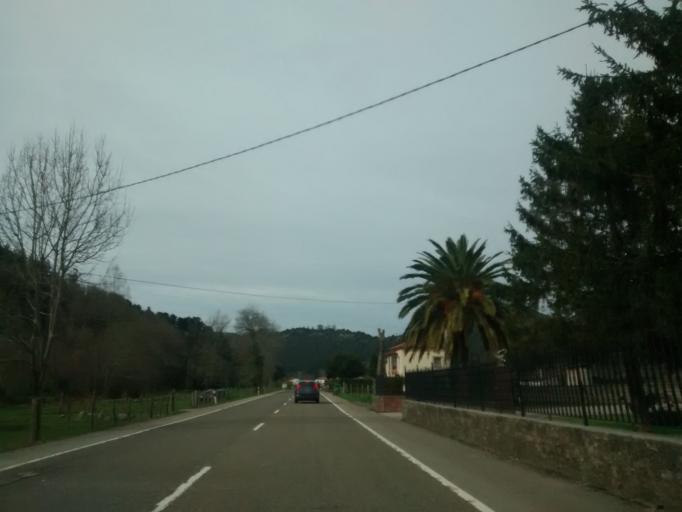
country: ES
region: Cantabria
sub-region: Provincia de Cantabria
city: Corvera
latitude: 43.2708
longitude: -3.9471
